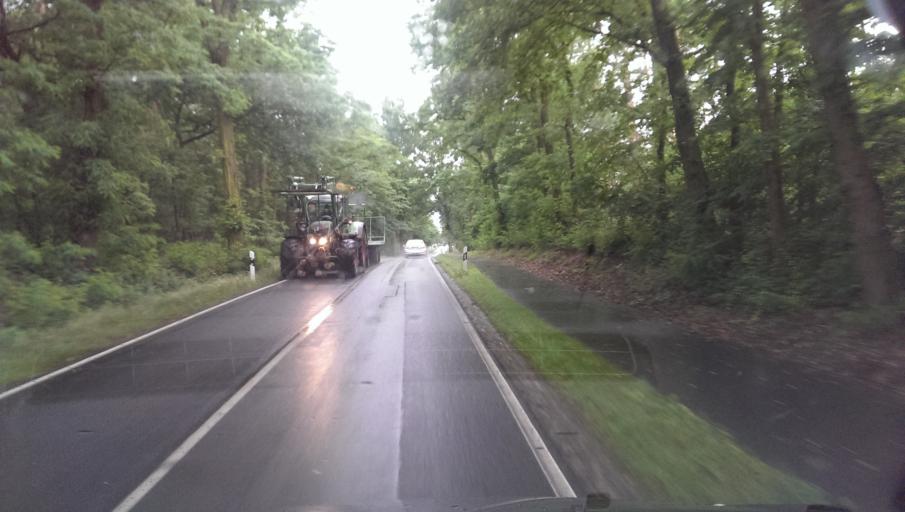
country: DE
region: Brandenburg
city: Gross Kreutz
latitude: 52.3742
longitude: 12.7181
